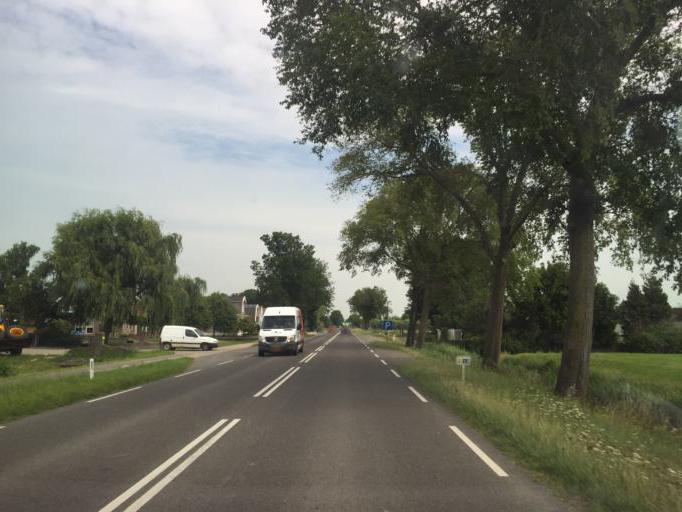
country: NL
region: North Holland
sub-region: Gemeente Beemster
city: Halfweg
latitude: 52.5905
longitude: 4.9384
